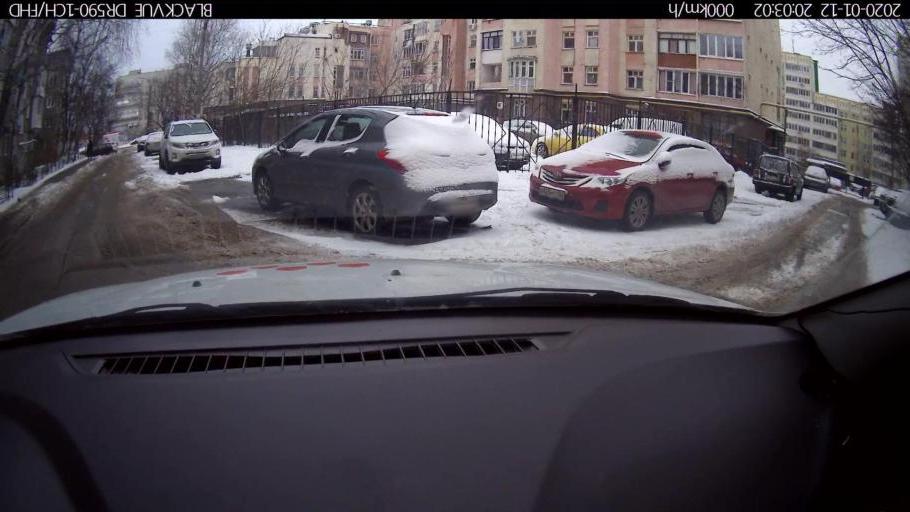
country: RU
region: Nizjnij Novgorod
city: Nizhniy Novgorod
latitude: 56.2869
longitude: 43.9366
